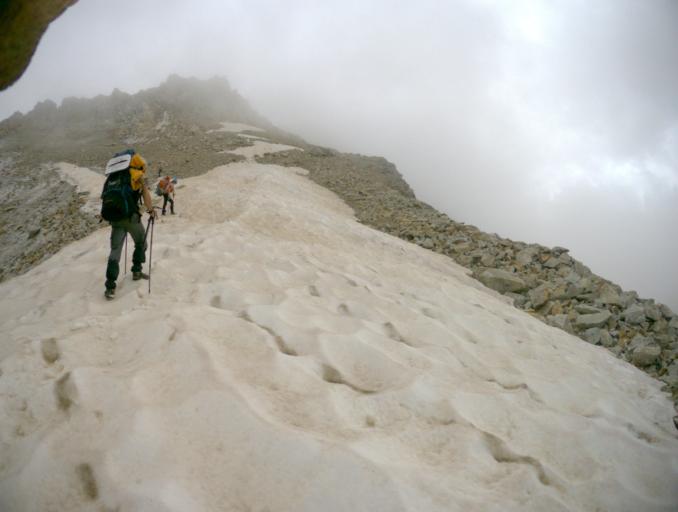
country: RU
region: Karachayevo-Cherkesiya
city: Uchkulan
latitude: 43.2785
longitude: 42.1124
